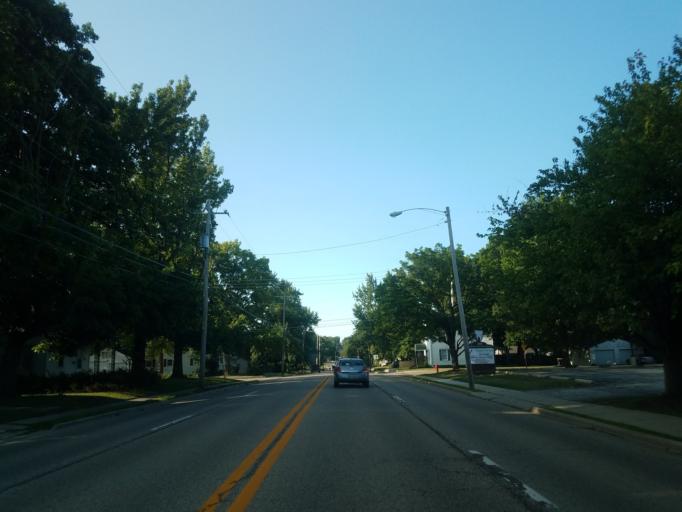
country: US
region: Illinois
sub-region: McLean County
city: Normal
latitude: 40.5073
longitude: -88.9823
